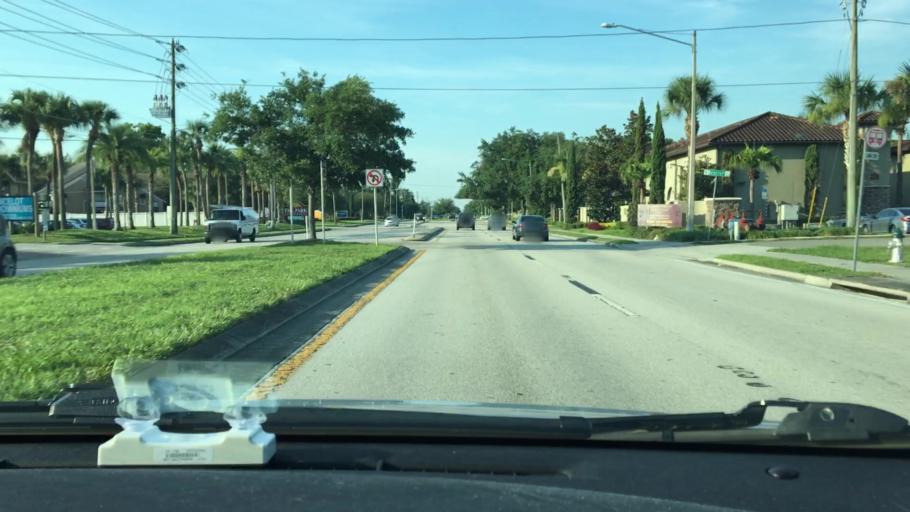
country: US
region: Florida
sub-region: Seminole County
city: Goldenrod
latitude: 28.5931
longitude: -81.2865
